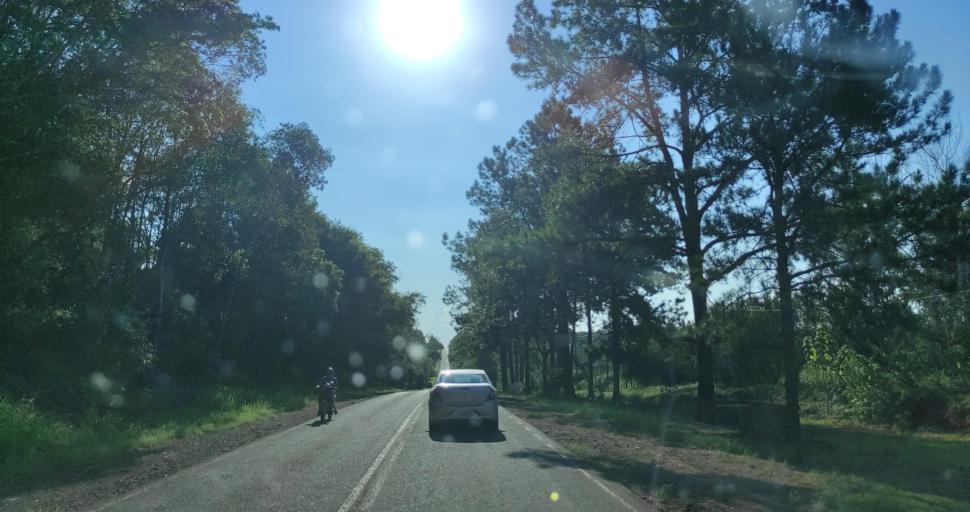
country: AR
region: Misiones
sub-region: Departamento de Eldorado
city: Eldorado
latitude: -26.4000
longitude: -54.4012
